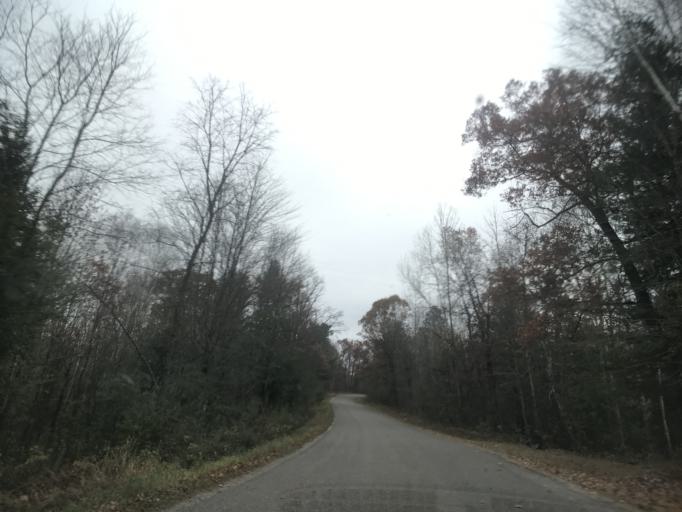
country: US
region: Michigan
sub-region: Dickinson County
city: Kingsford
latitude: 45.3835
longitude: -88.3217
